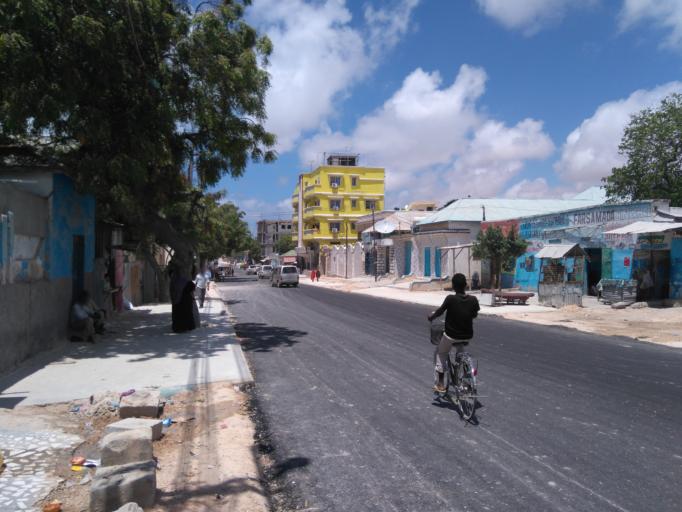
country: SO
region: Banaadir
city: Mogadishu
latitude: 2.0281
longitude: 45.3020
